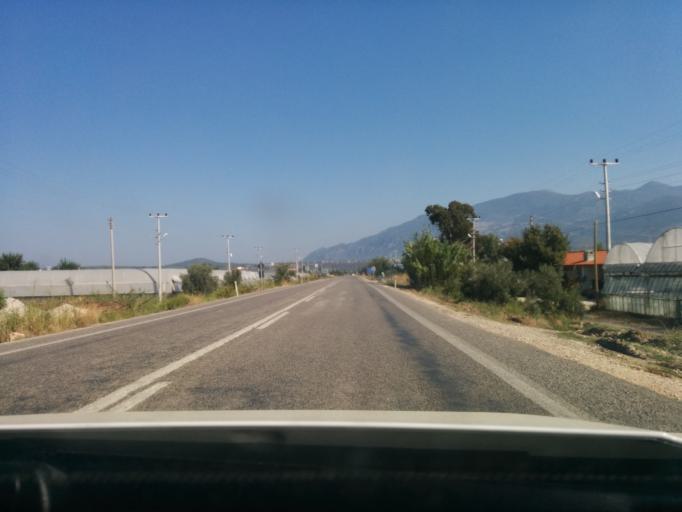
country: TR
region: Antalya
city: Kalkan
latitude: 36.3242
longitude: 29.3310
